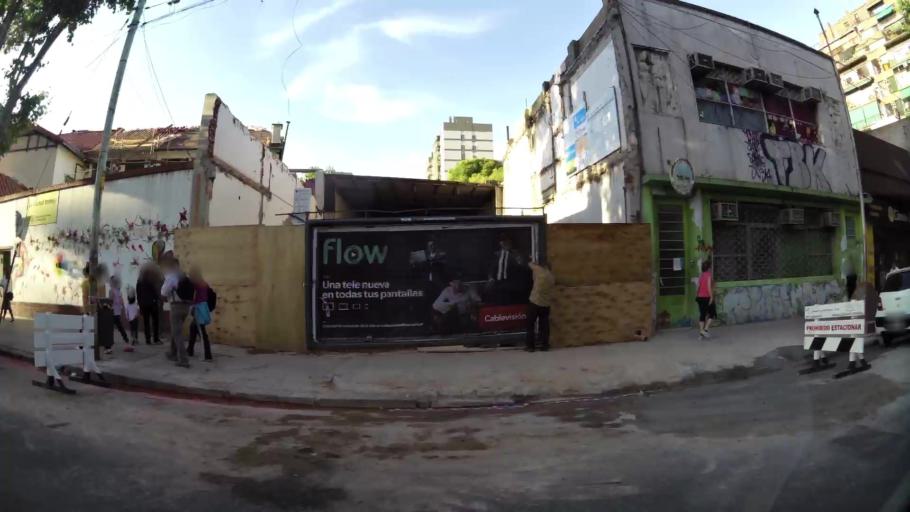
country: AR
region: Buenos Aires F.D.
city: Colegiales
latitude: -34.6087
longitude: -58.4325
